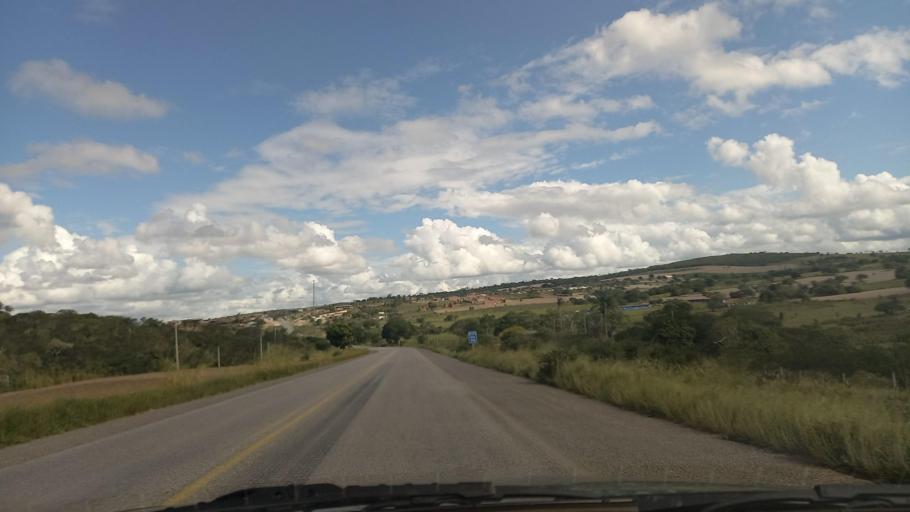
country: BR
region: Pernambuco
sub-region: Lajedo
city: Lajedo
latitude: -8.7442
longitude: -36.4312
